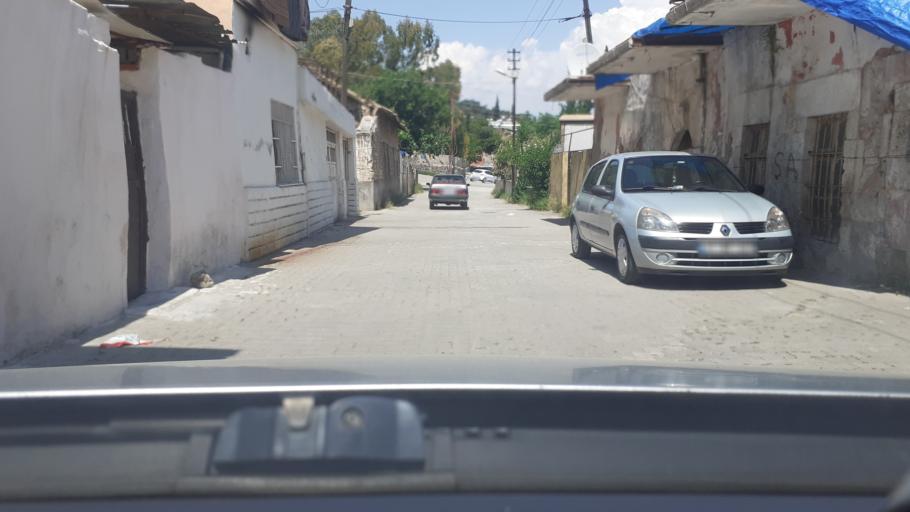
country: TR
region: Hatay
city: Kirikhan
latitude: 36.5006
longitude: 36.3524
